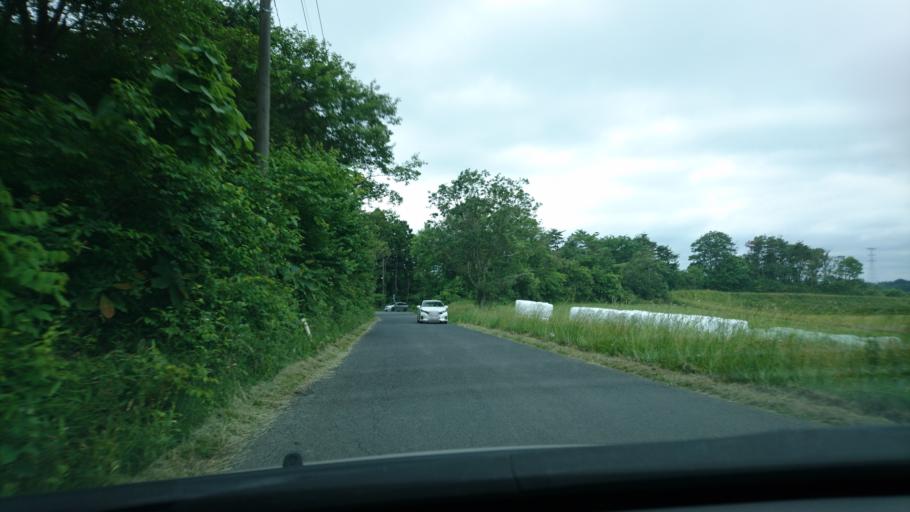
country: JP
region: Iwate
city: Ichinoseki
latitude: 38.8781
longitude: 141.2007
